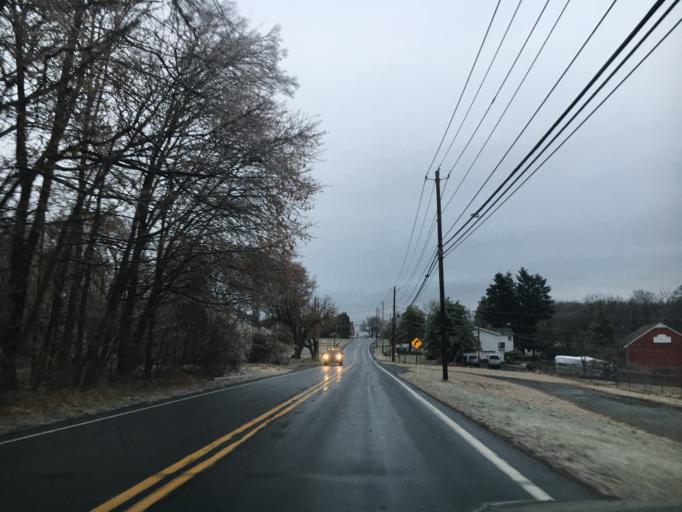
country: US
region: Pennsylvania
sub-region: Lehigh County
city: Schnecksville
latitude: 40.6185
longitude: -75.6414
